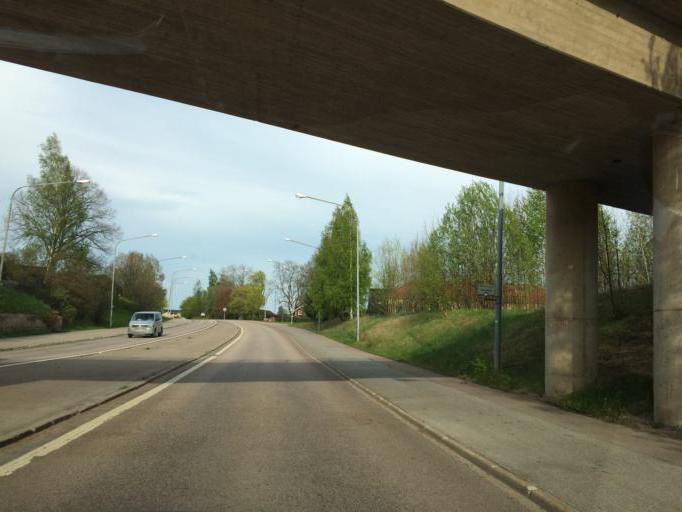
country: SE
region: Vaestmanland
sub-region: Hallstahammars Kommun
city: Hallstahammar
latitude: 59.6102
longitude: 16.2254
